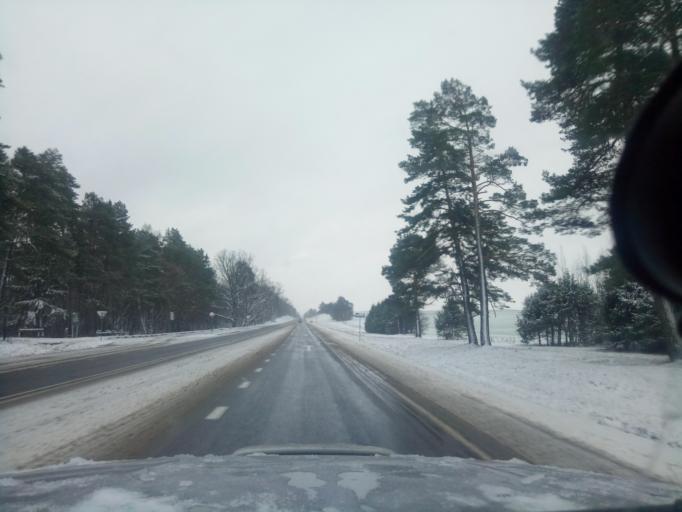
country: BY
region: Minsk
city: Haradzyeya
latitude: 53.2654
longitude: 26.6057
